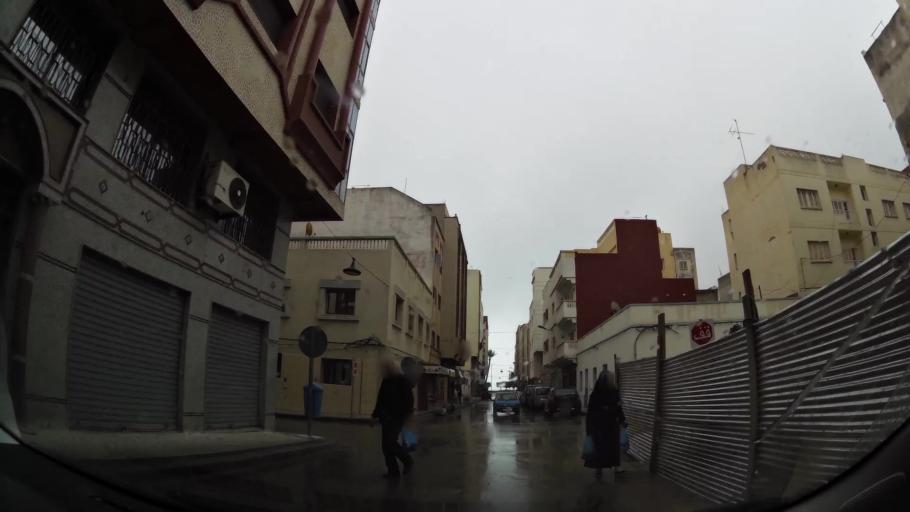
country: MA
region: Taza-Al Hoceima-Taounate
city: Al Hoceima
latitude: 35.2457
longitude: -3.9320
